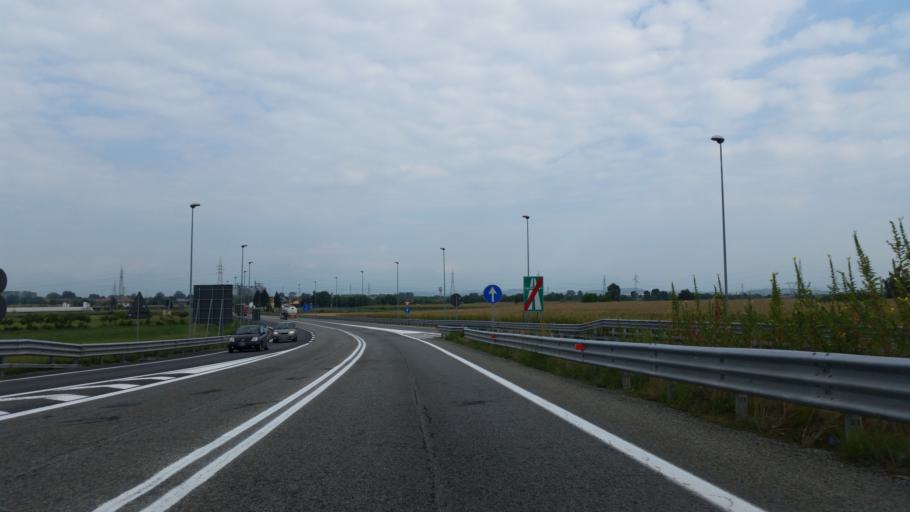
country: IT
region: Piedmont
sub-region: Provincia di Torino
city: Chivasso
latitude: 45.2239
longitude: 7.9184
